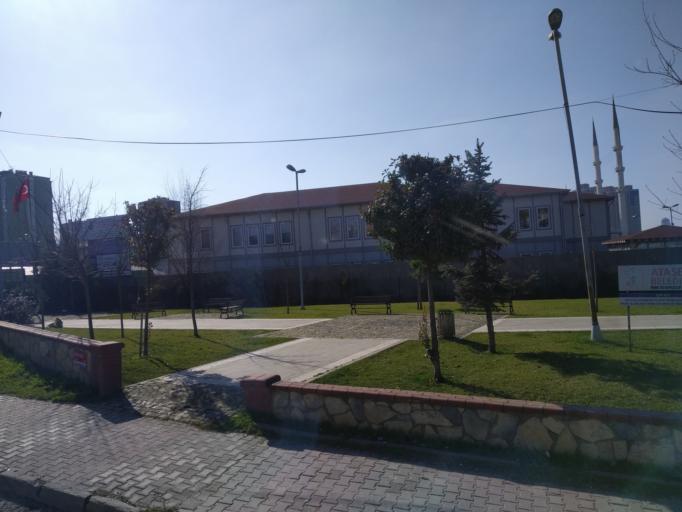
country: TR
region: Istanbul
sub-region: Atasehir
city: Atasehir
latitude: 40.9911
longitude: 29.1547
